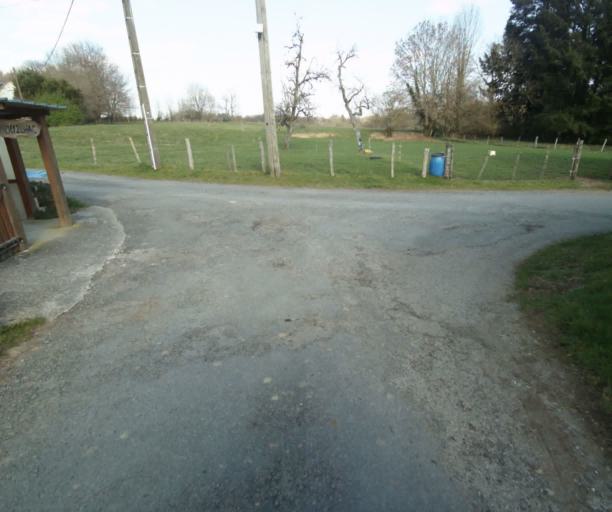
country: FR
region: Limousin
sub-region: Departement de la Correze
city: Saint-Mexant
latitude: 45.3389
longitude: 1.5948
